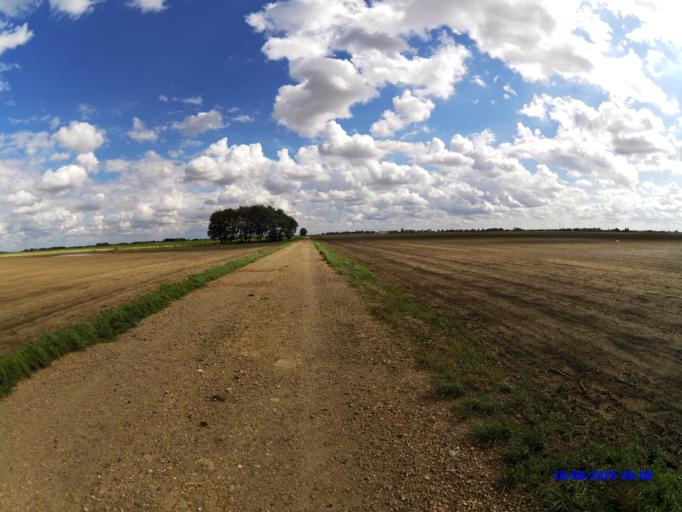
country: GB
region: England
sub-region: Cambridgeshire
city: Whittlesey
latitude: 52.5122
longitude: -0.0831
